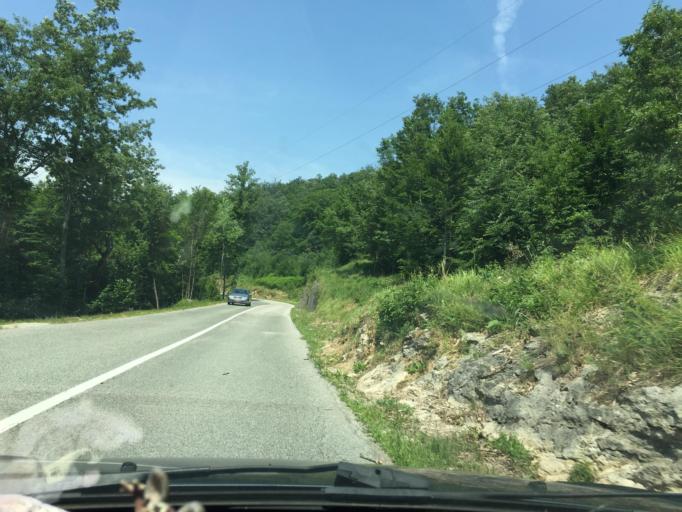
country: HR
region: Primorsko-Goranska
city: Matulji
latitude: 45.4146
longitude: 14.2442
